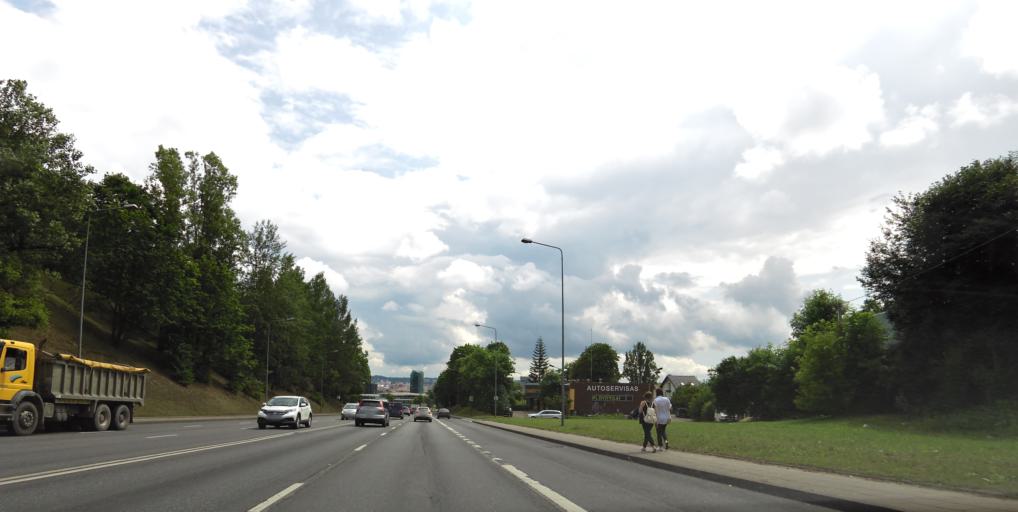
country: LT
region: Vilnius County
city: Seskine
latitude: 54.7057
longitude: 25.2555
